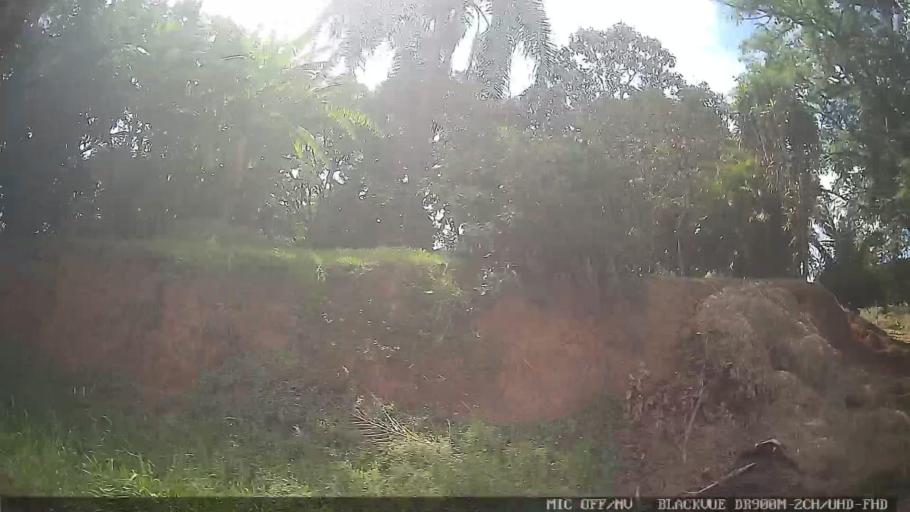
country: BR
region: Sao Paulo
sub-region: Braganca Paulista
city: Braganca Paulista
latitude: -22.9753
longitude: -46.6391
